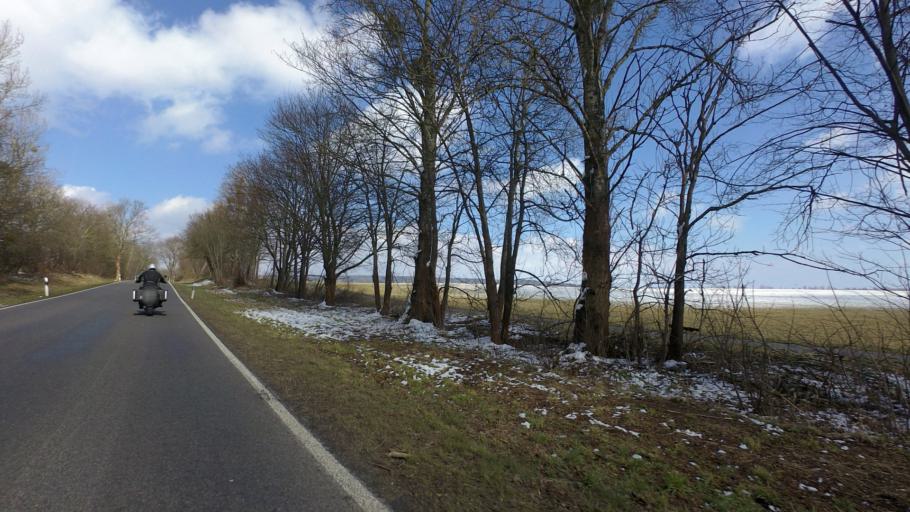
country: DE
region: Brandenburg
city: Britz
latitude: 52.8755
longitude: 13.7455
